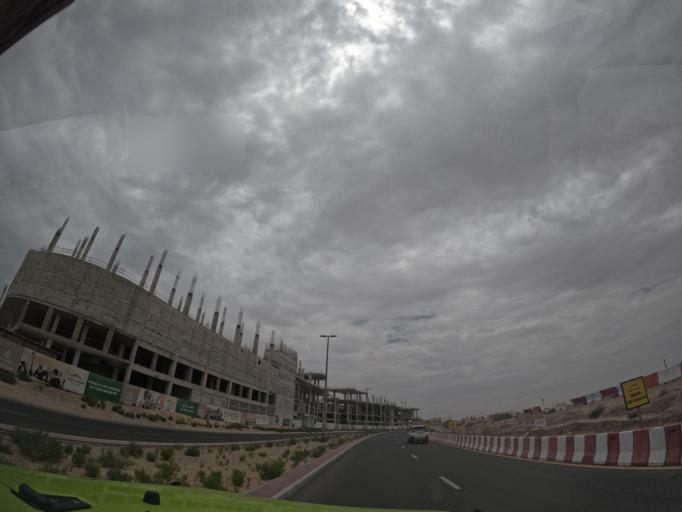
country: AE
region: Ash Shariqah
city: Sharjah
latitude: 25.1597
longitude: 55.3682
